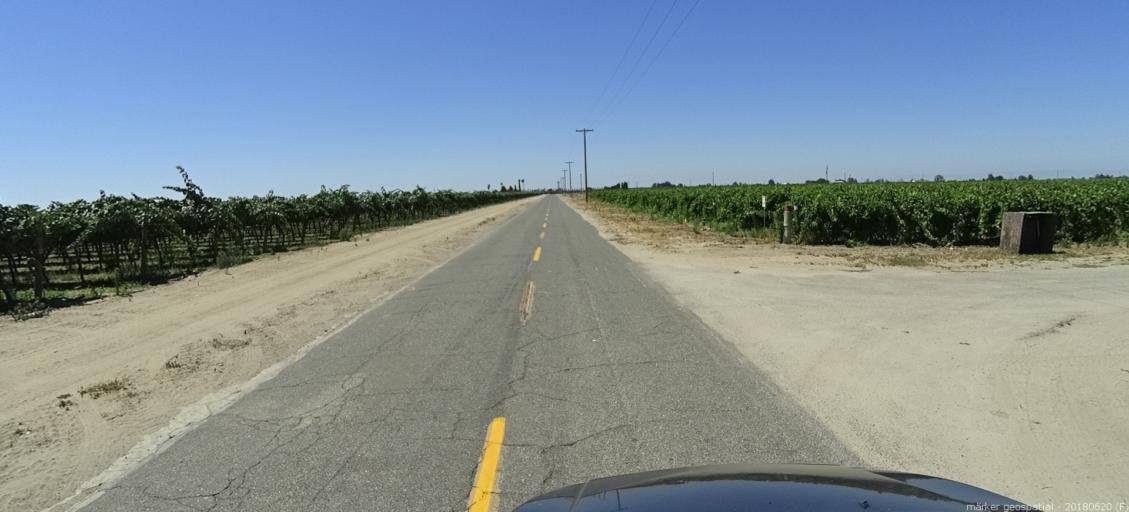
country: US
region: California
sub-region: Fresno County
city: Biola
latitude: 36.8417
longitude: -120.0010
